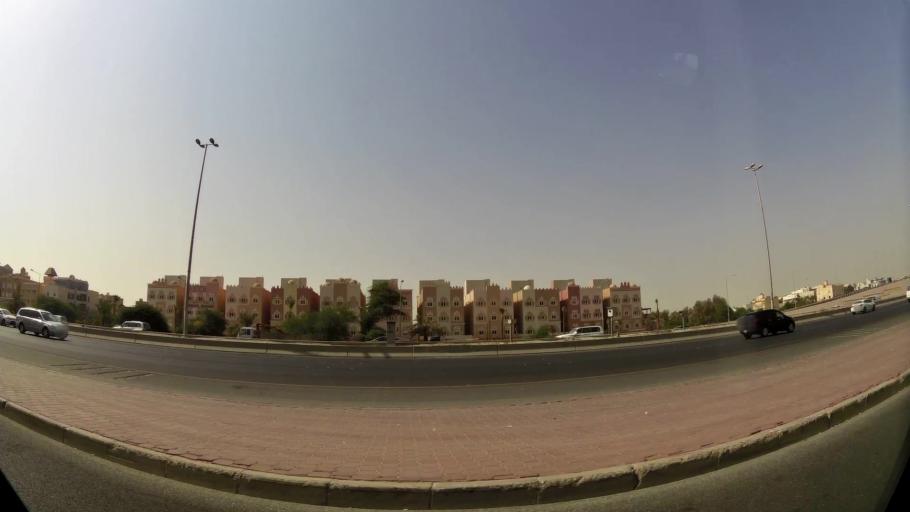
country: KW
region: Al Ahmadi
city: Al Fintas
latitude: 29.1823
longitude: 48.1135
